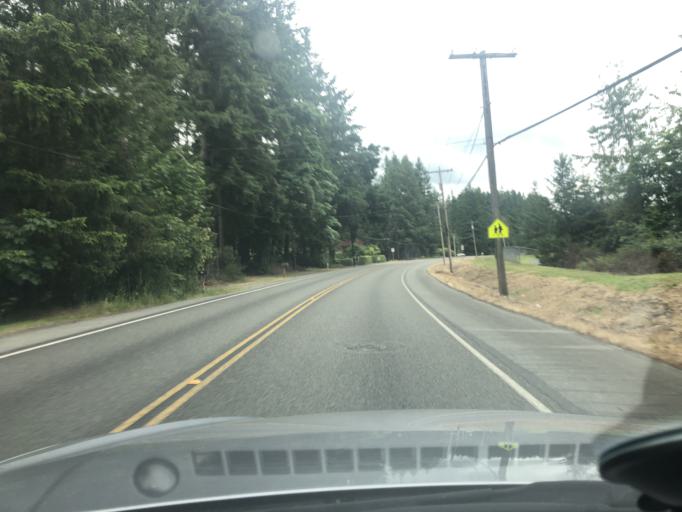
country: US
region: Washington
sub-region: King County
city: Black Diamond
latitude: 47.3257
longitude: -122.0402
